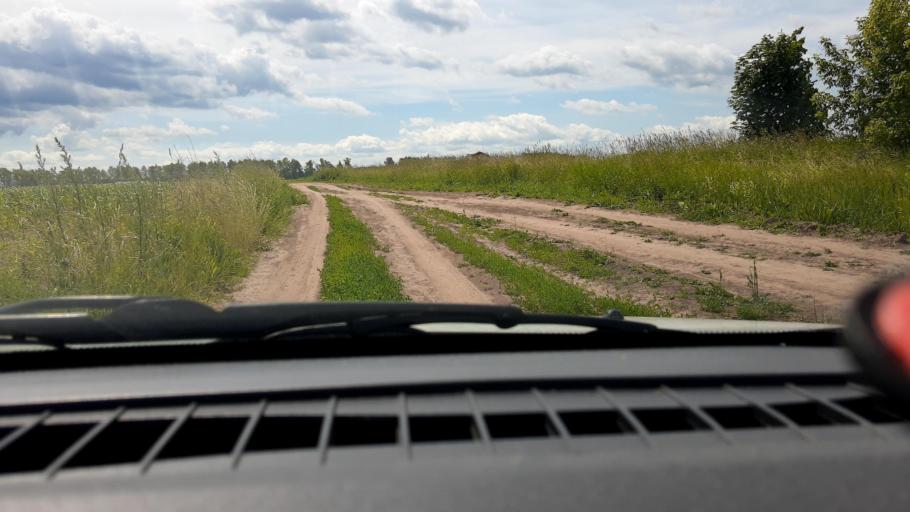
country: RU
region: Nizjnij Novgorod
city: Afonino
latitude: 56.1248
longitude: 44.0312
